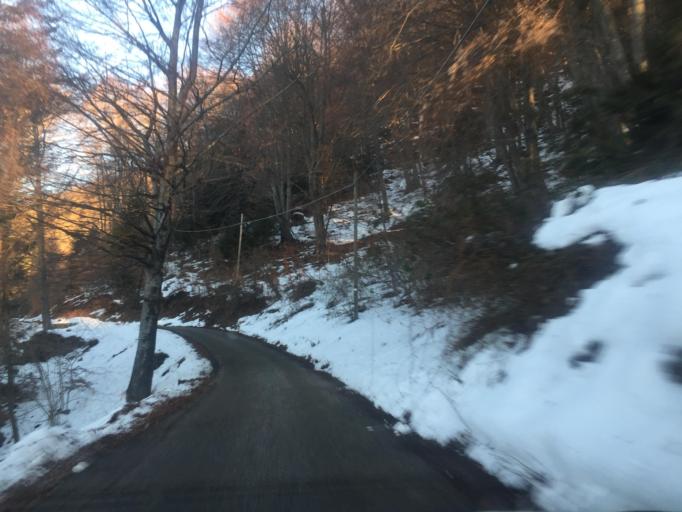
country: IT
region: Friuli Venezia Giulia
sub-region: Provincia di Udine
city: Lauco
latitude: 46.4425
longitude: 12.9402
